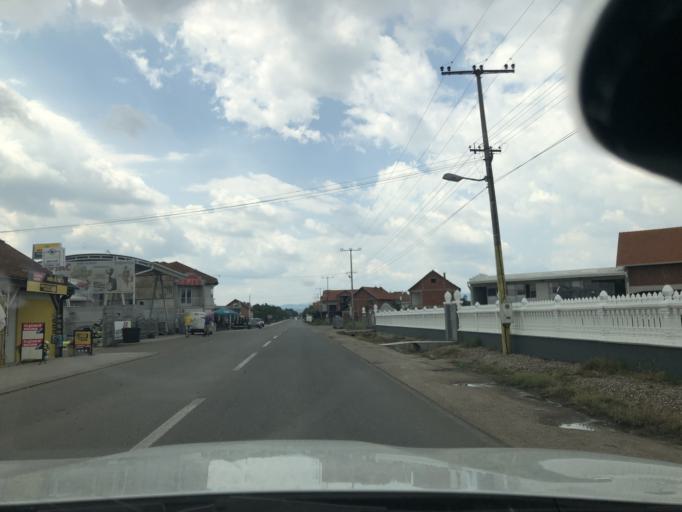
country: RS
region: Central Serbia
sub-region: Jablanicki Okrug
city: Lebane
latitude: 42.9560
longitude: 21.8331
